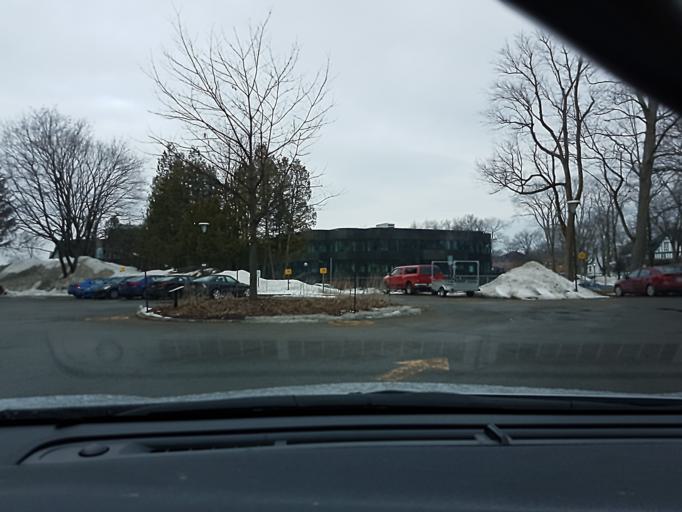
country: CA
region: Quebec
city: Quebec
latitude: 46.7956
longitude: -71.2326
